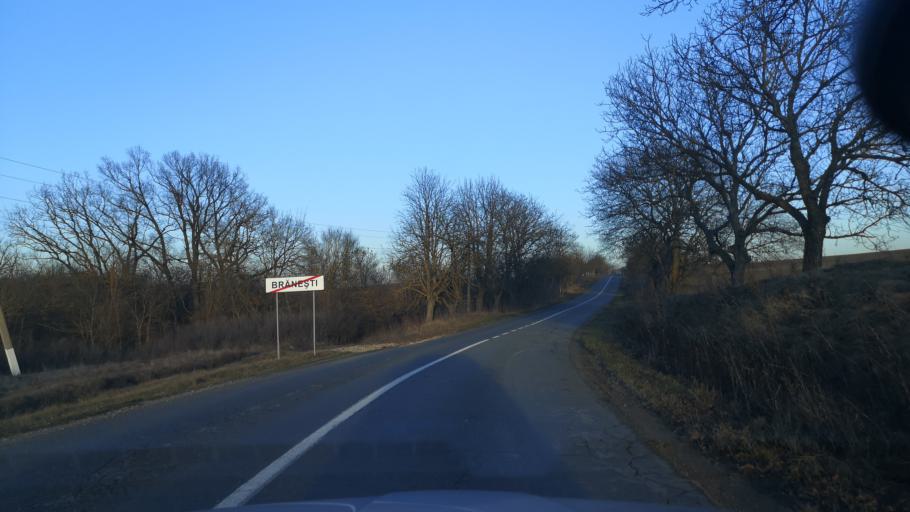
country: MD
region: Orhei
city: Orhei
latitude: 47.3095
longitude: 28.9388
